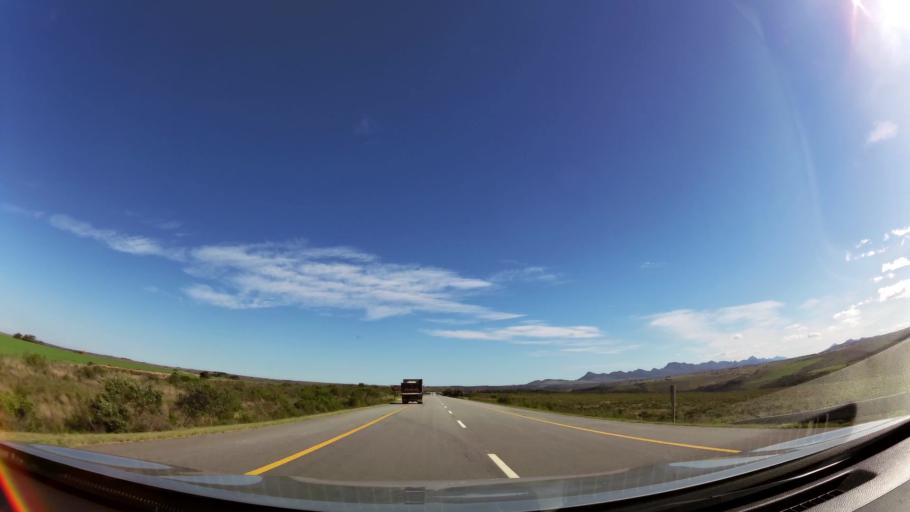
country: ZA
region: Eastern Cape
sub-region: Cacadu District Municipality
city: Kruisfontein
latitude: -34.0235
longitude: 24.6114
